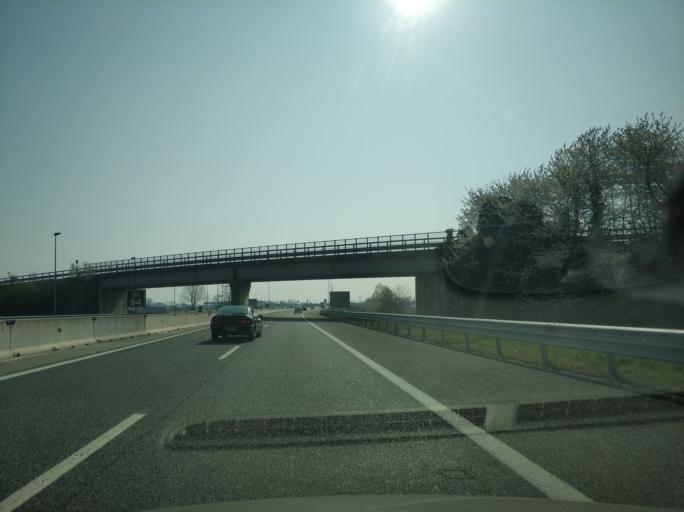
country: IT
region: Piedmont
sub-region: Provincia di Vercelli
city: Santhia
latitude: 45.3689
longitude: 8.1379
